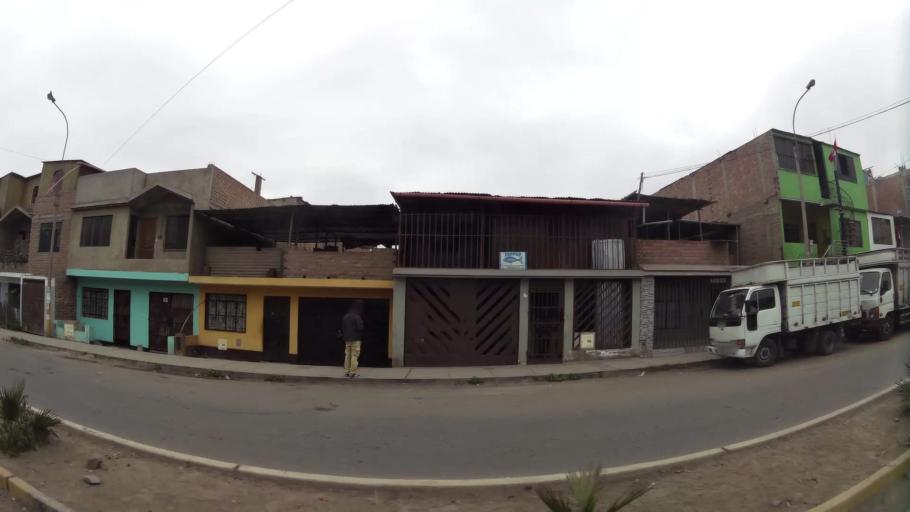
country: PE
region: Lima
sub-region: Lima
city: Surco
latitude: -12.2002
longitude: -76.9555
